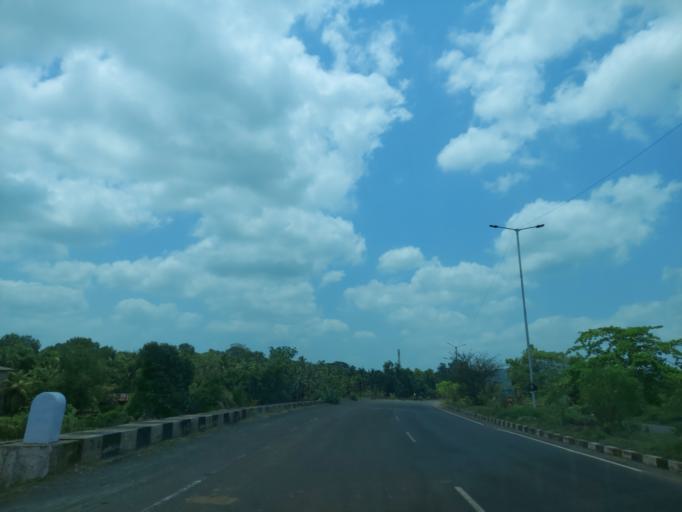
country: IN
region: Maharashtra
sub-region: Sindhudurg
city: Savantvadi
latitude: 15.8213
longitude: 73.8599
